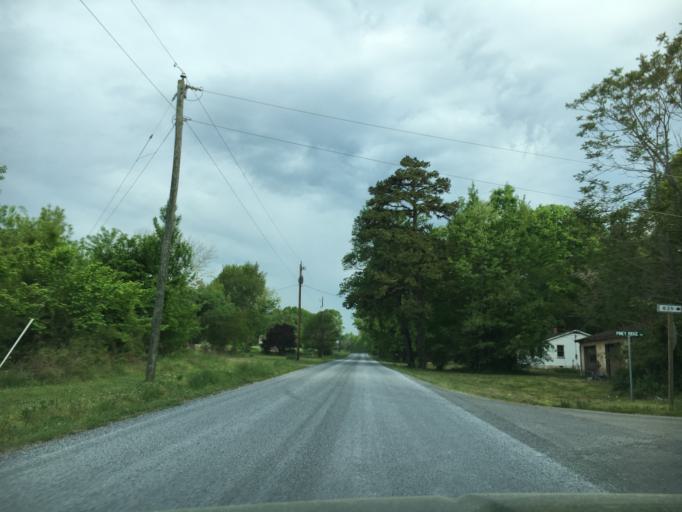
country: US
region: Virginia
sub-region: Campbell County
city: Brookneal
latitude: 36.9538
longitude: -78.9702
